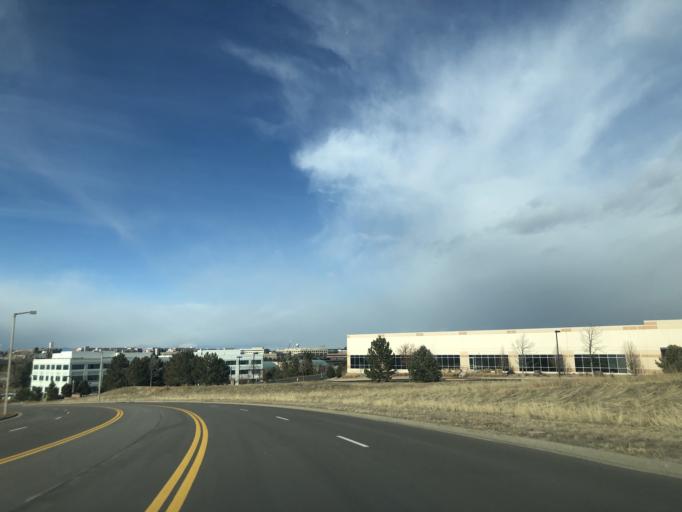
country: US
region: Colorado
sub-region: Douglas County
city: Meridian
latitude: 39.5576
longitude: -104.8577
